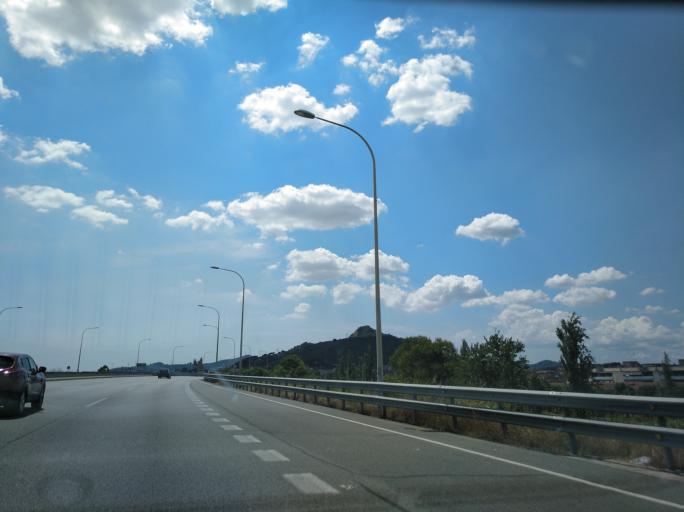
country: ES
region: Catalonia
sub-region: Provincia de Barcelona
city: Montcada i Reixac
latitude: 41.4936
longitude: 2.1902
